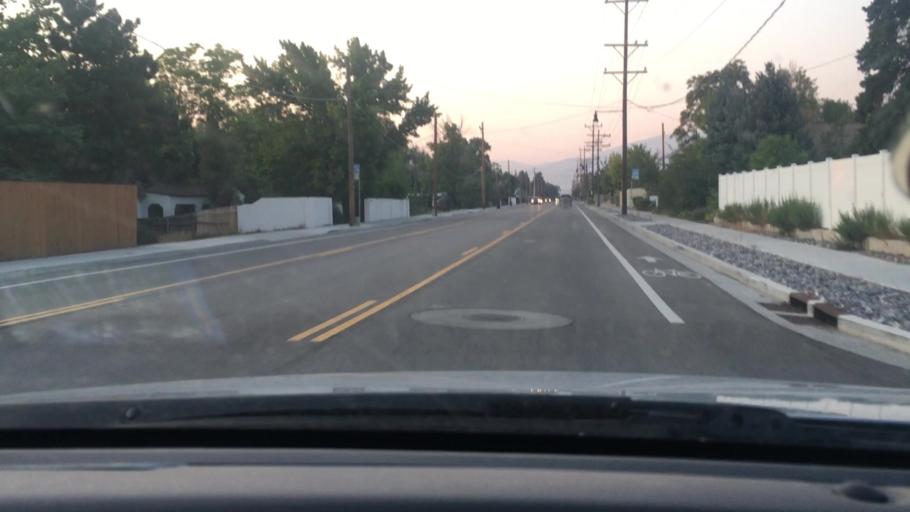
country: US
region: Utah
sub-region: Salt Lake County
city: East Millcreek
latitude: 40.6884
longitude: -111.8244
